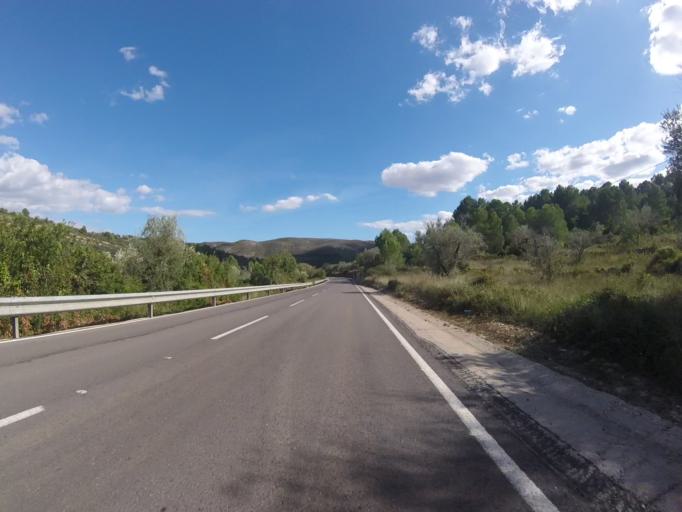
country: ES
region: Valencia
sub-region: Provincia de Castello
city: Cuevas de Vinroma
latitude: 40.3052
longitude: 0.1608
